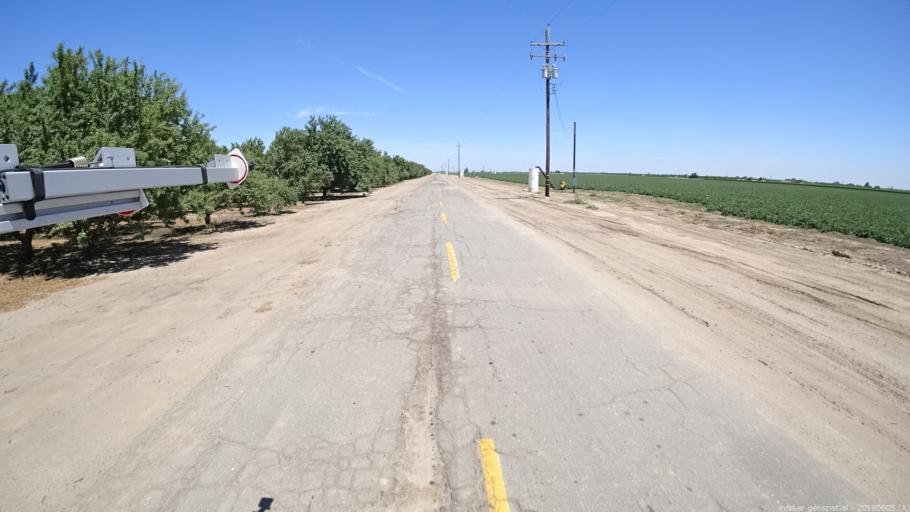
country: US
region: California
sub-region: Madera County
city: Chowchilla
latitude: 37.0906
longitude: -120.3977
